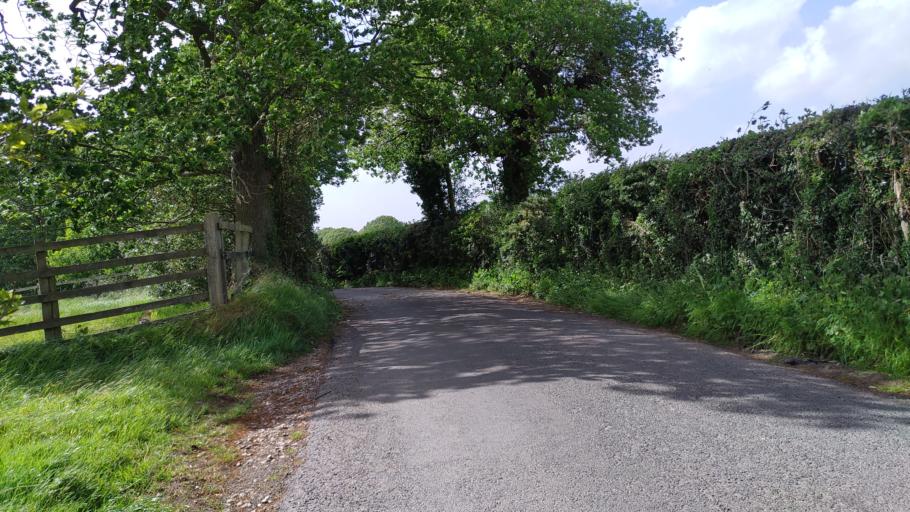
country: GB
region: England
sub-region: Lancashire
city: Chorley
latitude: 53.6449
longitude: -2.5908
